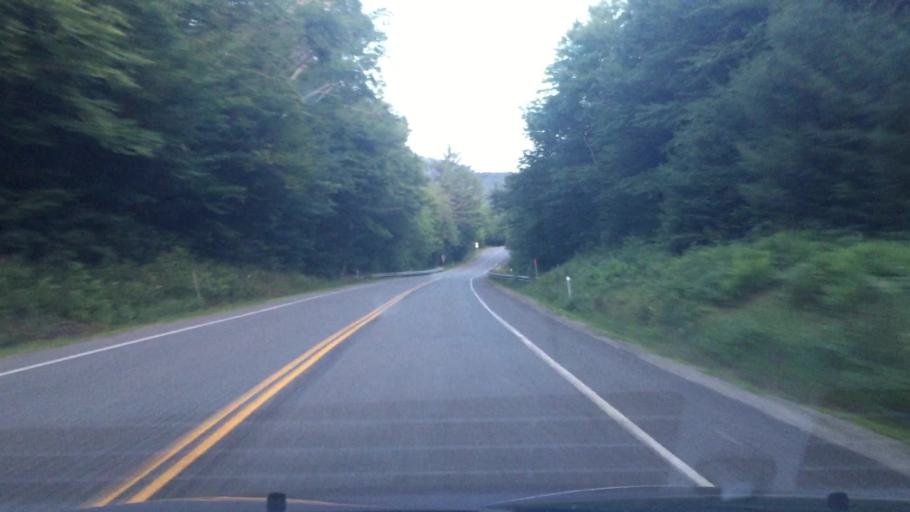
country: US
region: New Hampshire
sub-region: Grafton County
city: Woodstock
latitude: 44.0455
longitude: -71.5565
